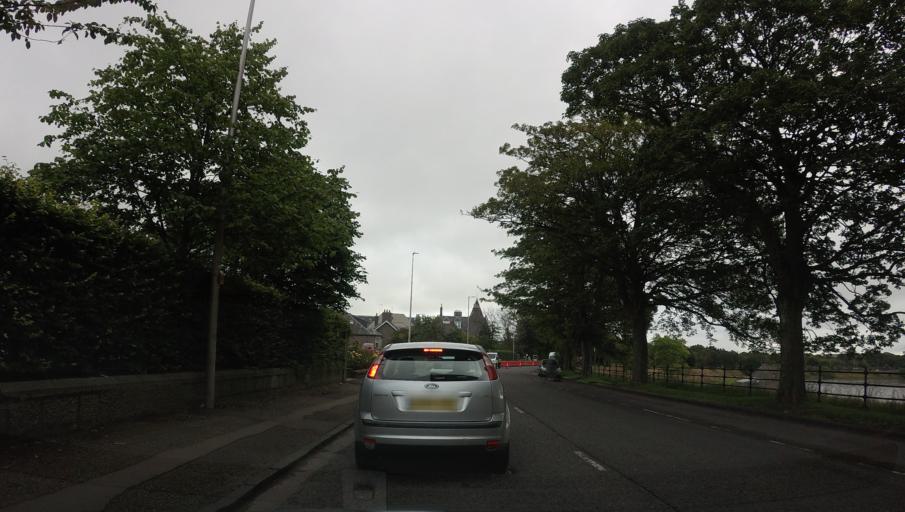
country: GB
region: Scotland
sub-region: Aberdeen City
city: Aberdeen
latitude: 57.1277
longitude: -2.1167
